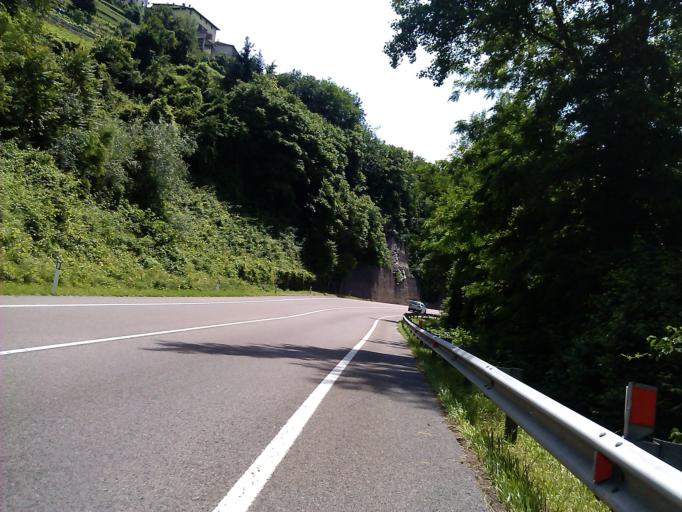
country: IT
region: Trentino-Alto Adige
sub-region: Provincia di Trento
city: Tenna
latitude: 46.0339
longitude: 11.2446
